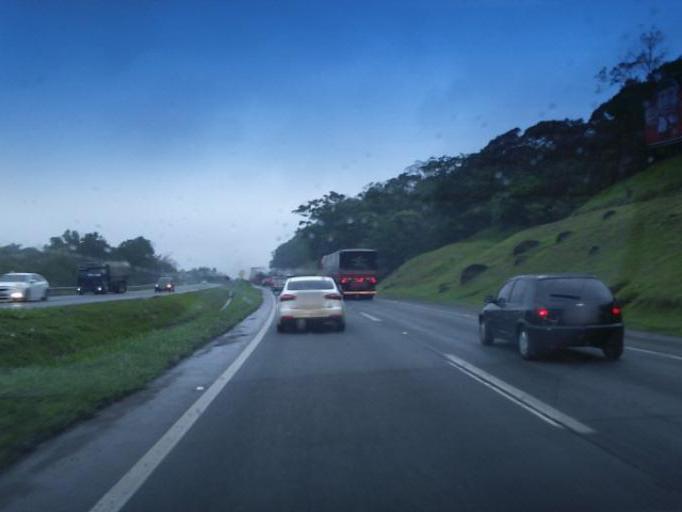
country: BR
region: Santa Catarina
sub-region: Joinville
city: Joinville
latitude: -26.0051
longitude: -48.8702
